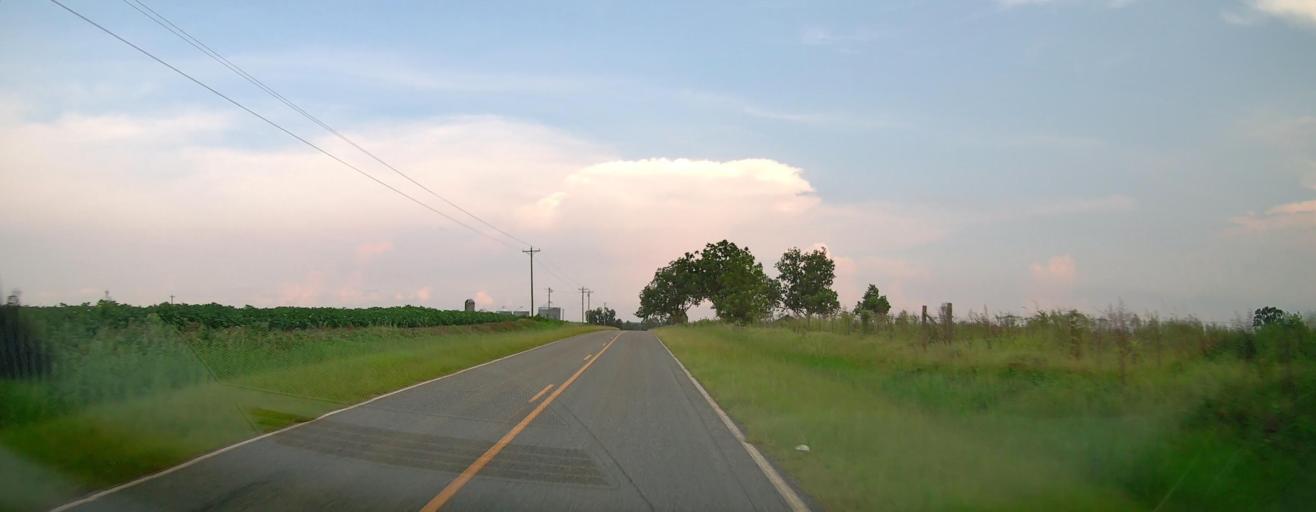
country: US
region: Georgia
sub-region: Laurens County
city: East Dublin
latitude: 32.6442
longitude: -82.8177
